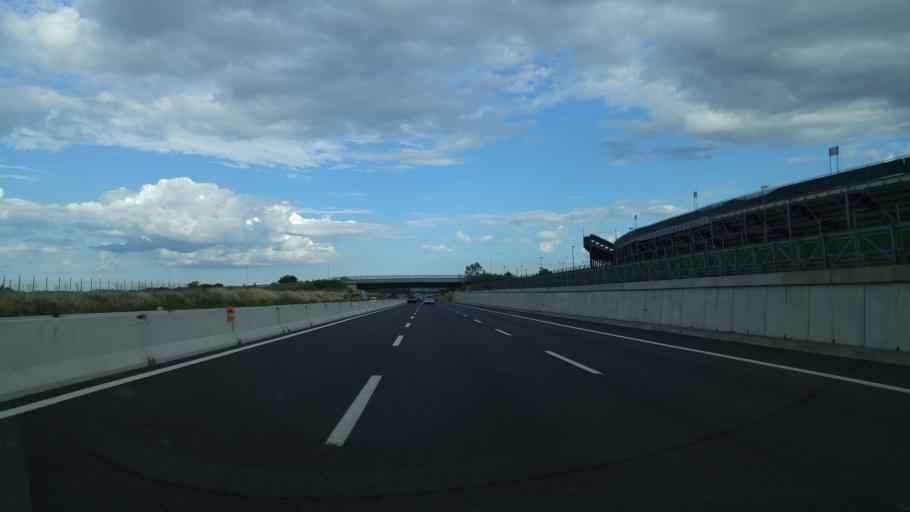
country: IT
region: Emilia-Romagna
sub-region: Provincia di Rimini
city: Santa Monica-Cella
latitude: 43.9653
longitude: 12.6893
